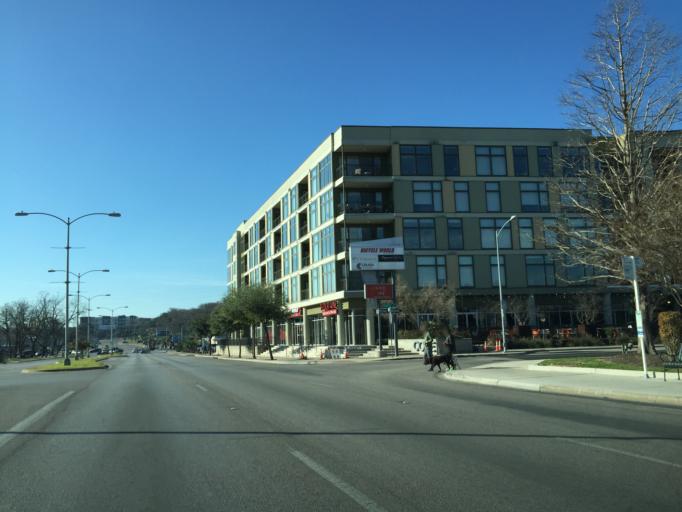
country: US
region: Texas
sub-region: Travis County
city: Austin
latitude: 30.2633
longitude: -97.7577
